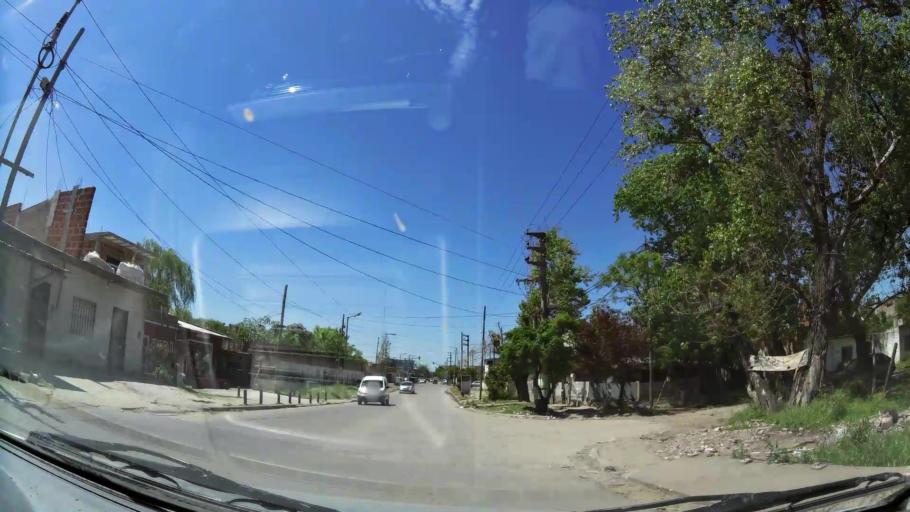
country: AR
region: Buenos Aires
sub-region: Partido de Quilmes
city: Quilmes
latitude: -34.7244
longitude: -58.3144
